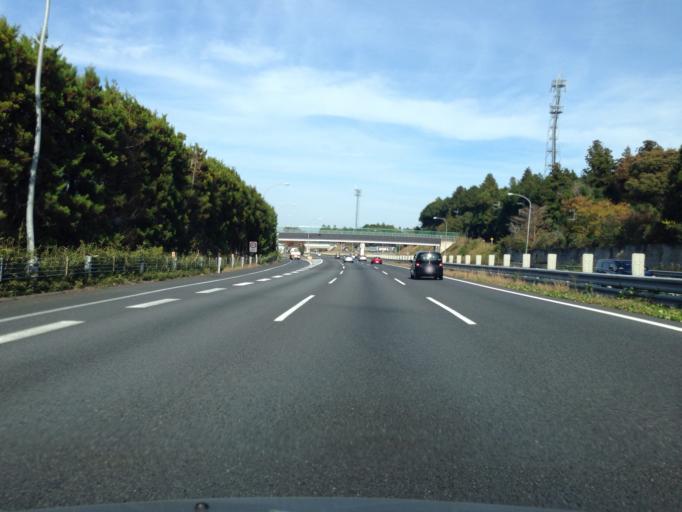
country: JP
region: Ibaraki
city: Ishioka
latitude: 36.2321
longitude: 140.2958
